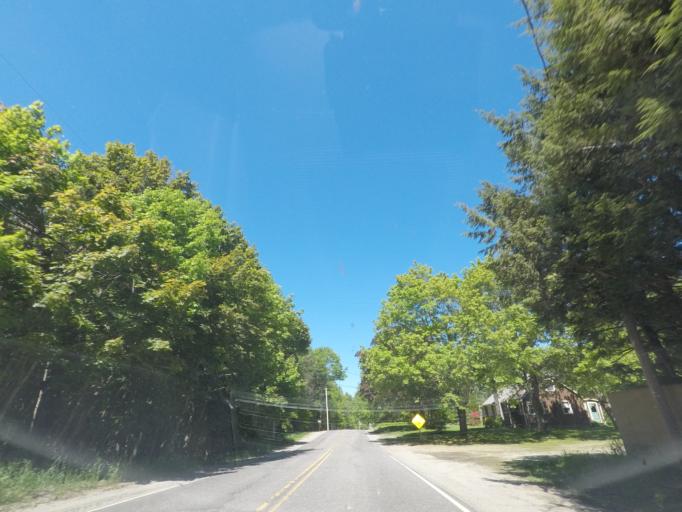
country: US
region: Maine
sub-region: Kennebec County
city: Gardiner
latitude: 44.2269
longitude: -69.8557
